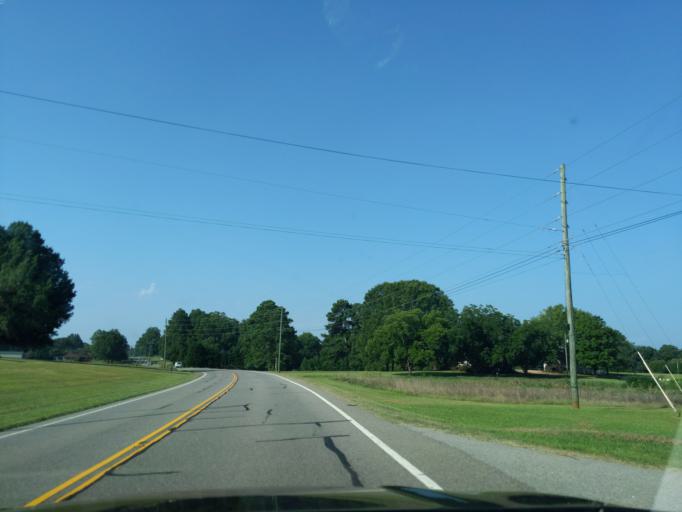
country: US
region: South Carolina
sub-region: Newberry County
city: Prosperity
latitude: 34.1377
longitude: -81.5393
